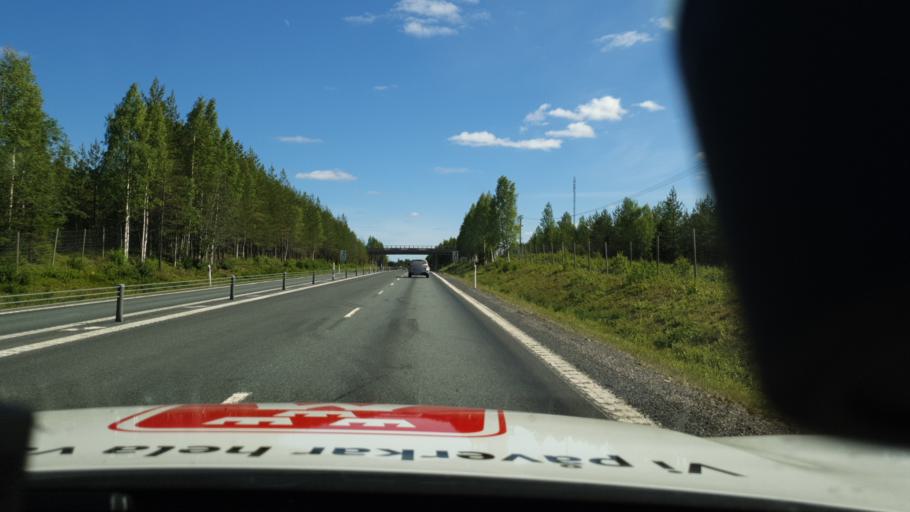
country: SE
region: Norrbotten
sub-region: Haparanda Kommun
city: Haparanda
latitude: 65.8270
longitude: 23.7907
